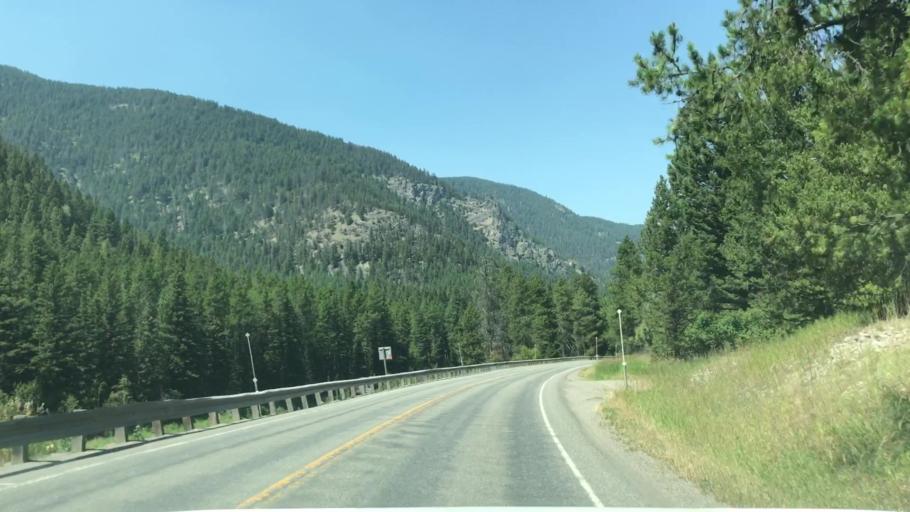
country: US
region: Montana
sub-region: Gallatin County
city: Big Sky
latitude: 45.3987
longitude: -111.2154
